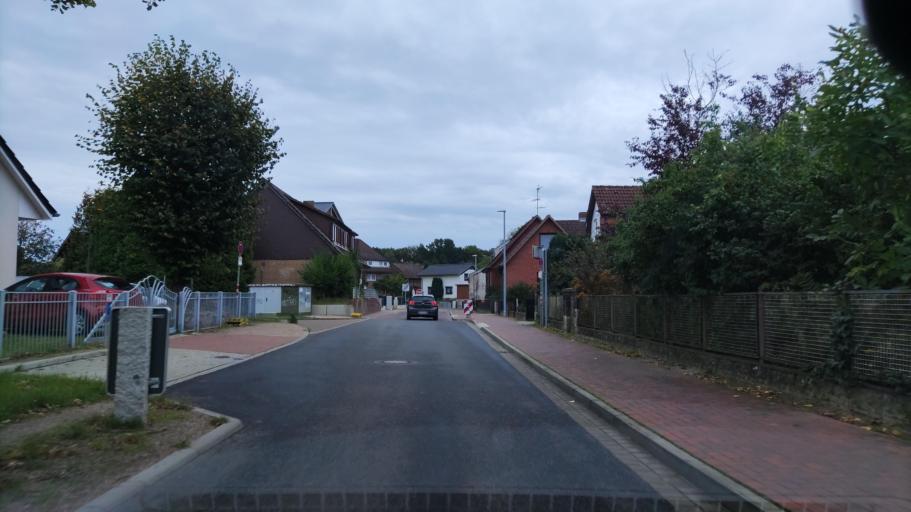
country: DE
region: Schleswig-Holstein
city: Trittau
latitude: 53.6043
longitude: 10.4107
